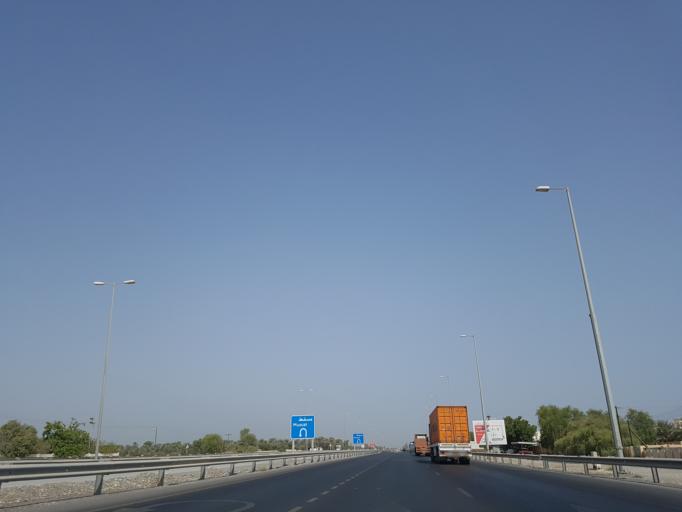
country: OM
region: Al Batinah
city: As Suwayq
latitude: 23.7610
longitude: 57.5554
